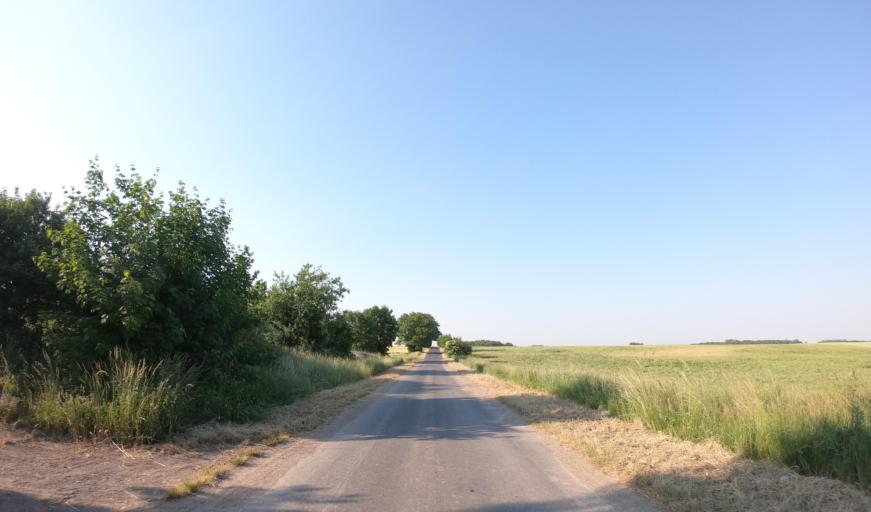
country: PL
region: West Pomeranian Voivodeship
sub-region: Powiat lobeski
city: Radowo Male
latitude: 53.6404
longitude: 15.4036
